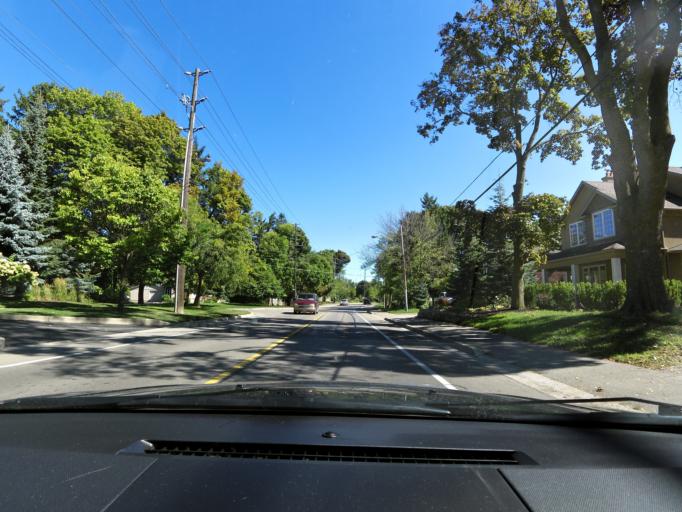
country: CA
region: Ontario
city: Hamilton
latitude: 43.3144
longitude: -79.8130
